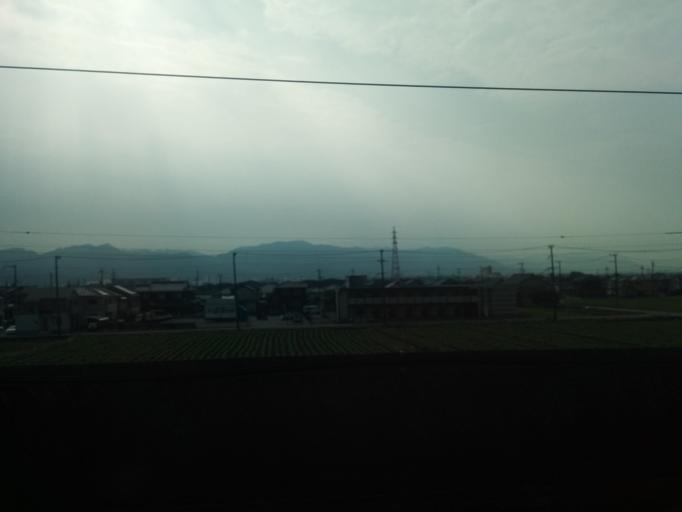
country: JP
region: Shiga Prefecture
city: Youkaichi
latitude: 35.1844
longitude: 136.2200
